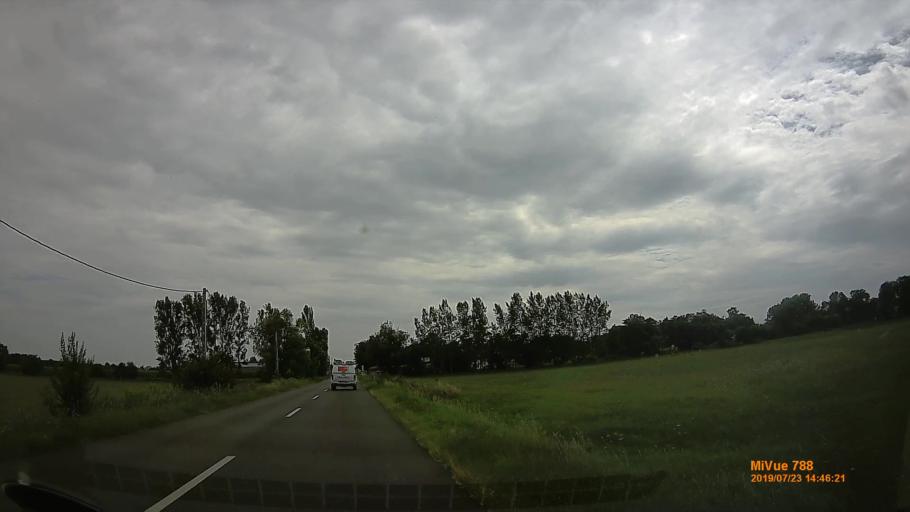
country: HU
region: Szabolcs-Szatmar-Bereg
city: Nyiregyhaza
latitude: 47.9197
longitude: 21.6766
